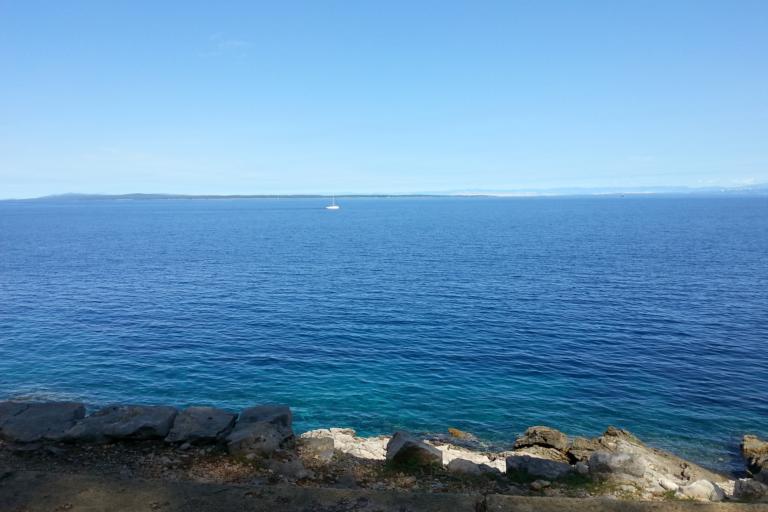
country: HR
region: Primorsko-Goranska
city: Mali Losinj
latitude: 44.5252
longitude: 14.4932
